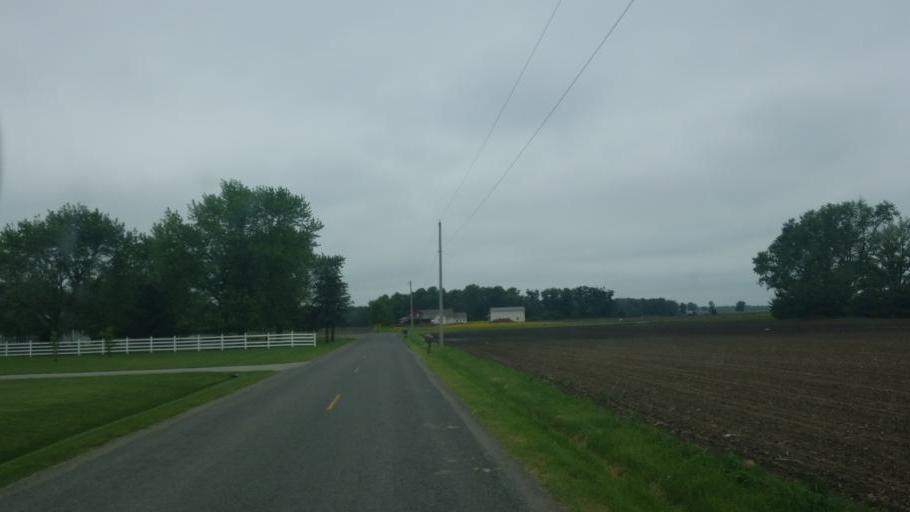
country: US
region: Indiana
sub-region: Elkhart County
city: Nappanee
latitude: 41.4572
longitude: -86.0478
